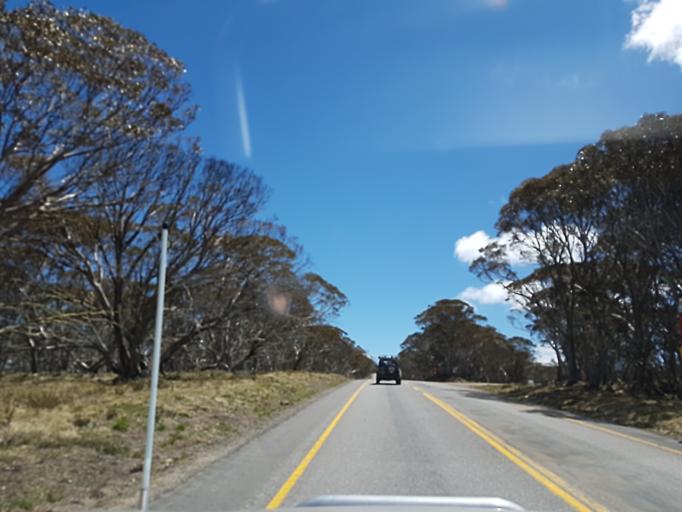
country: AU
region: Victoria
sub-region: Alpine
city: Mount Beauty
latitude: -37.0049
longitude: 147.1840
